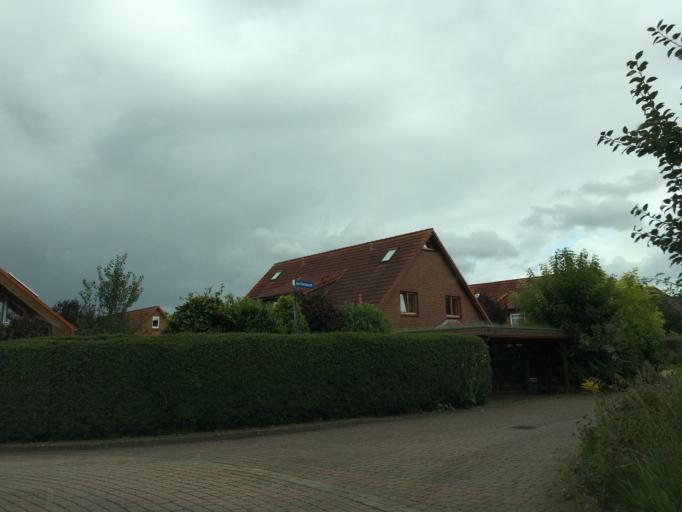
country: DE
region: Lower Saxony
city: Melbeck
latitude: 53.2137
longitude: 10.3908
